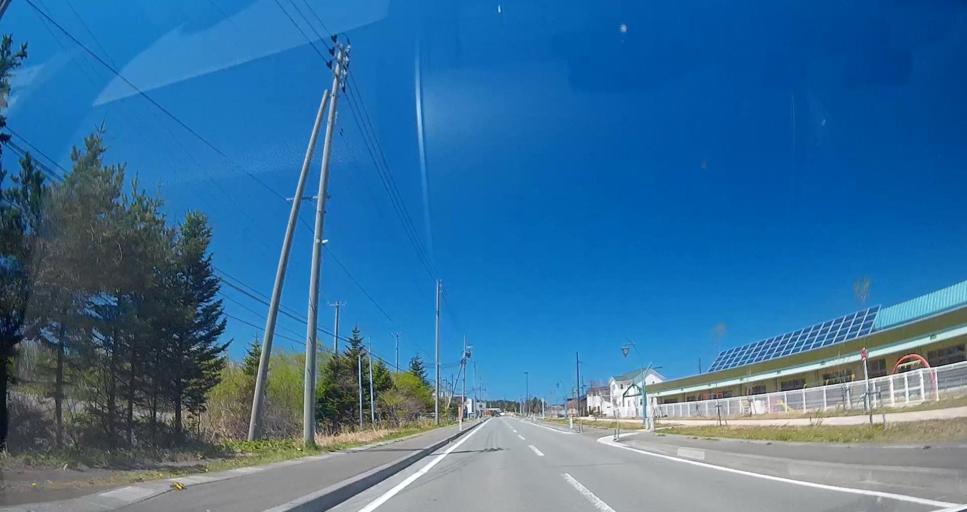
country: JP
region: Aomori
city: Misawa
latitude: 40.9687
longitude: 141.3657
